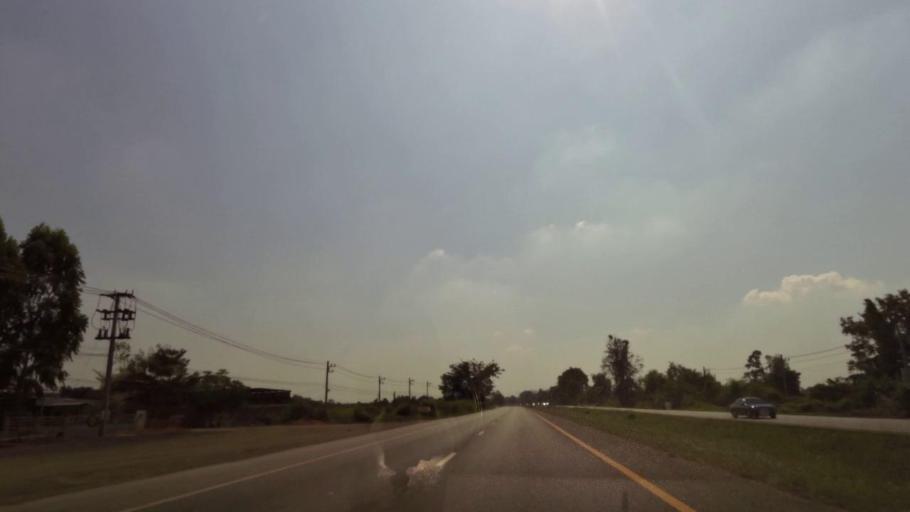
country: TH
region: Phichit
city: Bueng Na Rang
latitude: 16.2476
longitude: 100.1257
